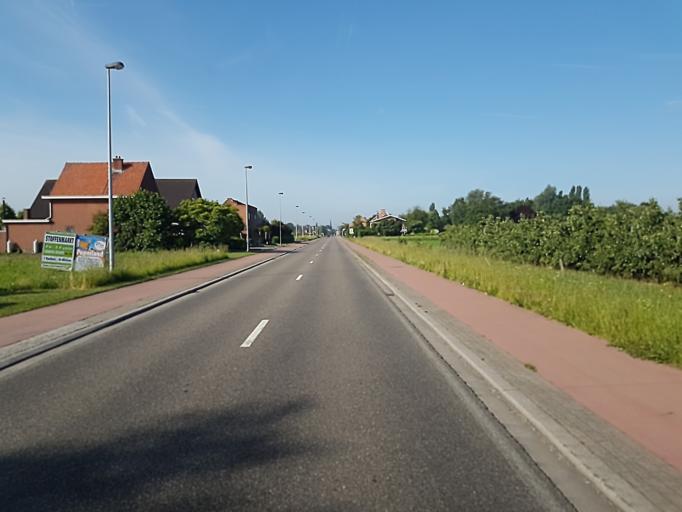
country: BE
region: Flanders
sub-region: Provincie Oost-Vlaanderen
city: Sint-Niklaas
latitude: 51.2033
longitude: 4.1903
